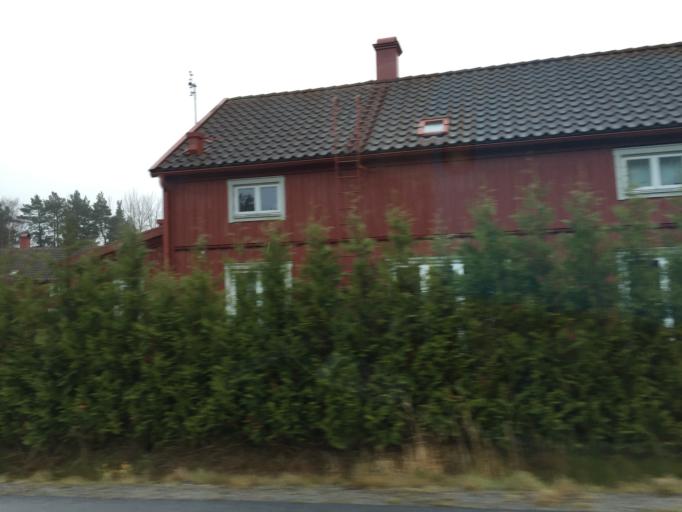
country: SE
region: Stockholm
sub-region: Nynashamns Kommun
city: Osmo
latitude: 59.0275
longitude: 17.9332
